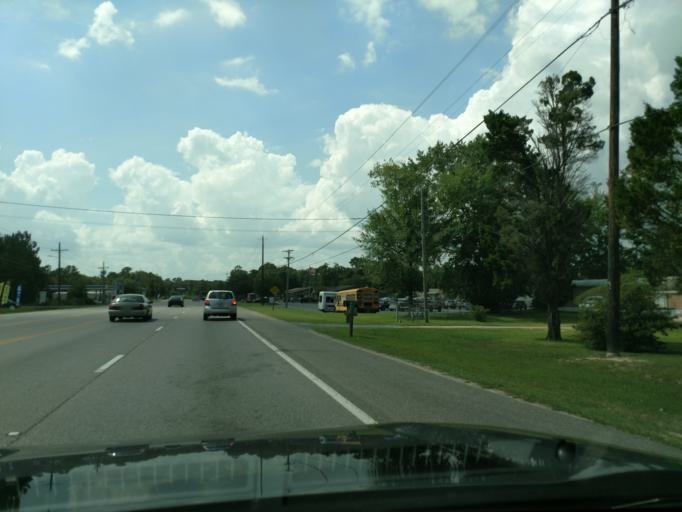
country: US
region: Mississippi
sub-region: Jackson County
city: Gulf Hills
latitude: 30.4406
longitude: -88.8359
